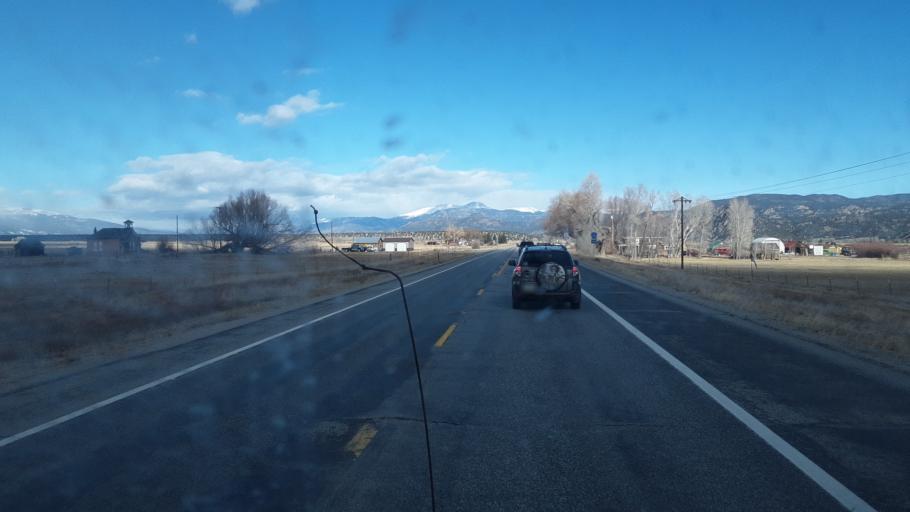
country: US
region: Colorado
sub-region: Chaffee County
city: Buena Vista
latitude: 38.7212
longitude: -106.0861
